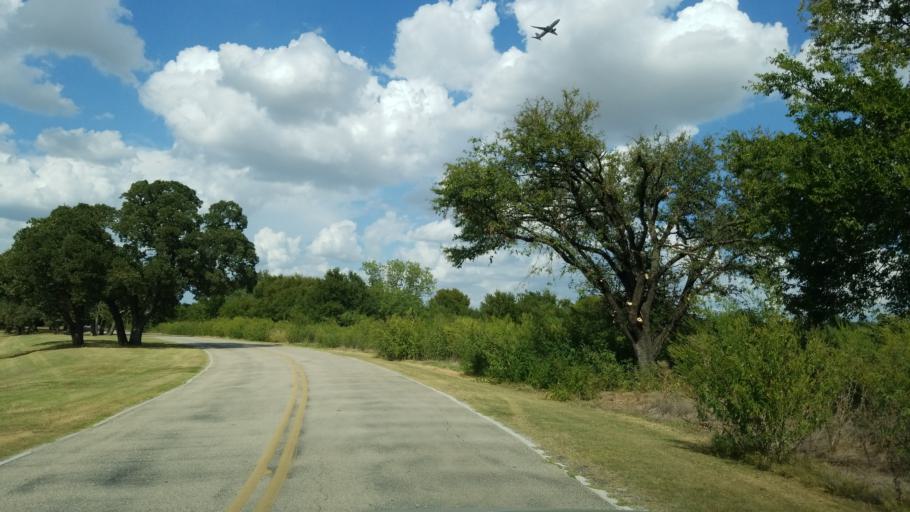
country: US
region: Texas
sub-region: Tarrant County
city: Euless
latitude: 32.8639
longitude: -97.0562
